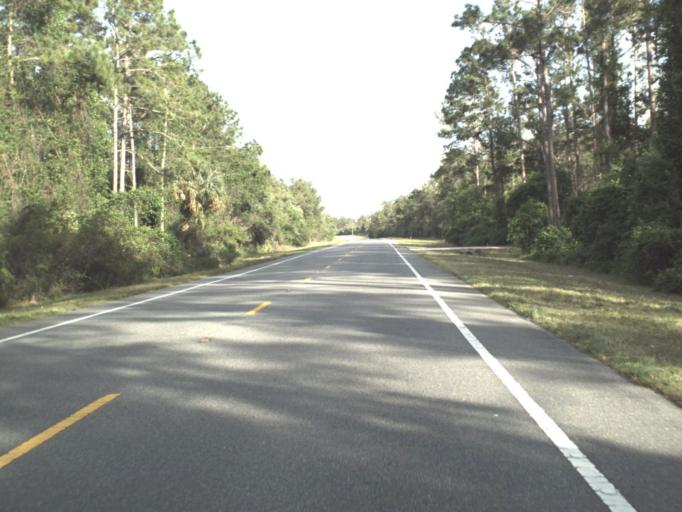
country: US
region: Florida
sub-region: Lake County
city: Astor
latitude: 29.1638
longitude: -81.6069
